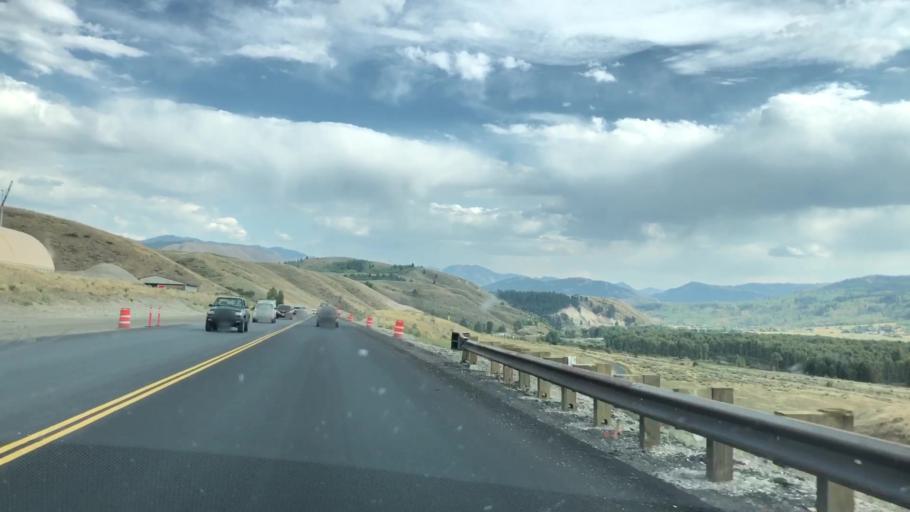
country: US
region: Wyoming
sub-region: Teton County
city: South Park
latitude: 43.4032
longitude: -110.7565
